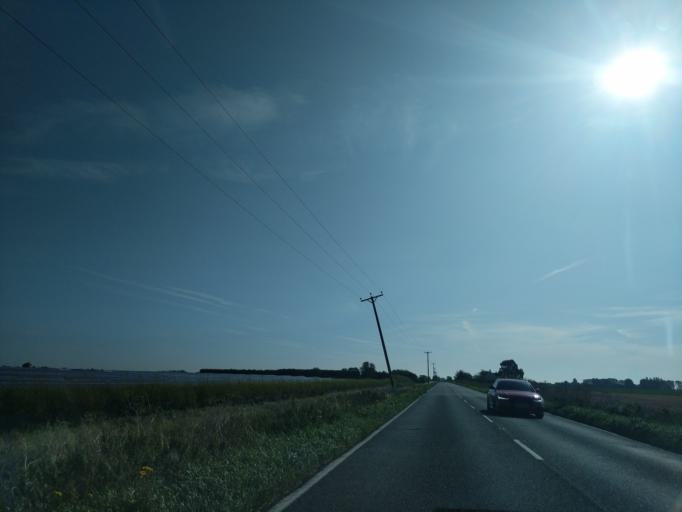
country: GB
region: England
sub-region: Lincolnshire
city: Bourne
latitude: 52.7721
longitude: -0.3218
